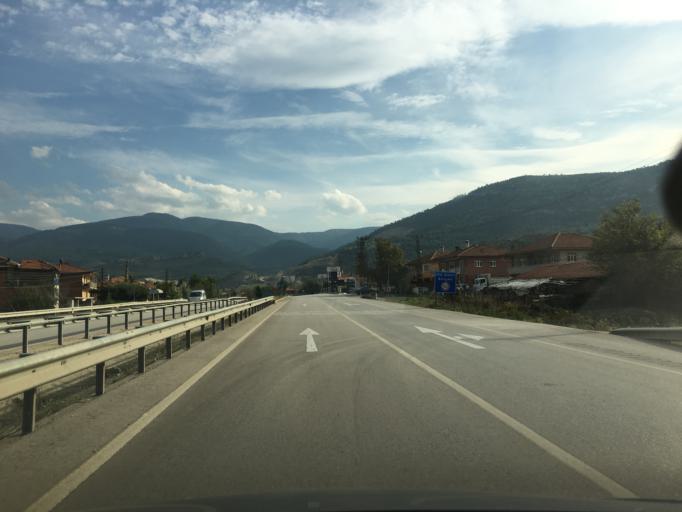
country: TR
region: Karabuk
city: Karabuk
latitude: 41.1055
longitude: 32.6688
